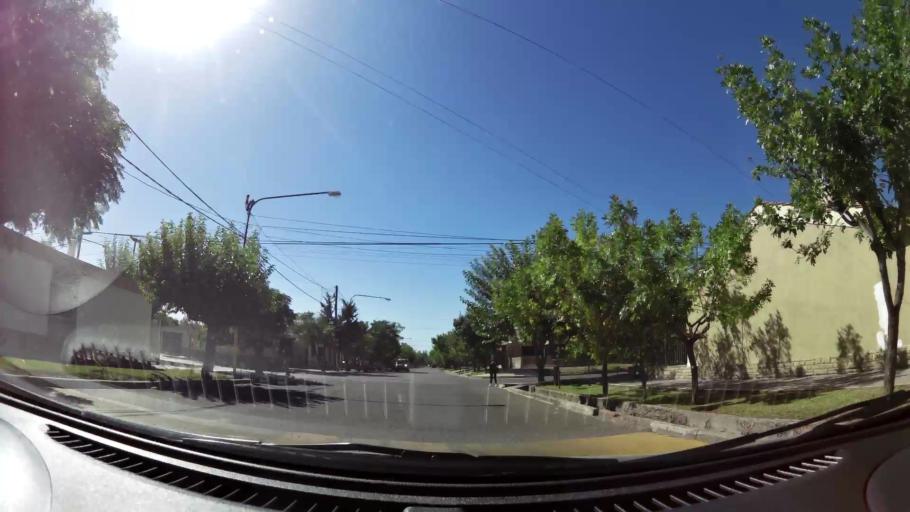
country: AR
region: Mendoza
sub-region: Departamento de Maipu
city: Maipu
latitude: -32.9724
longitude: -68.7977
